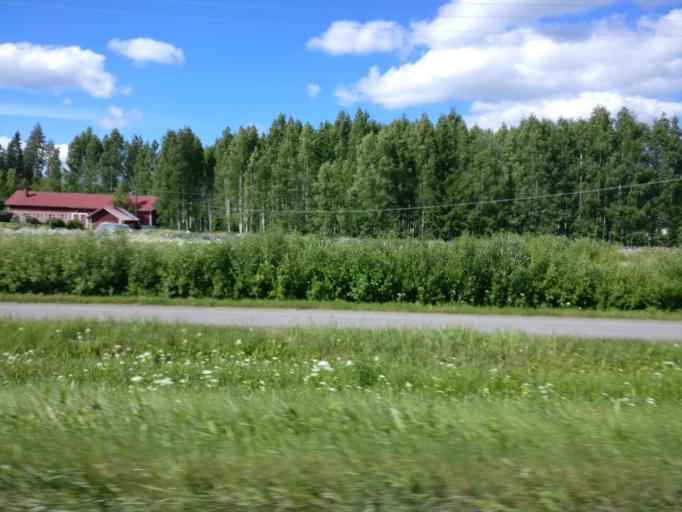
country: FI
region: Southern Savonia
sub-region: Savonlinna
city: Savonlinna
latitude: 61.8773
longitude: 28.9893
